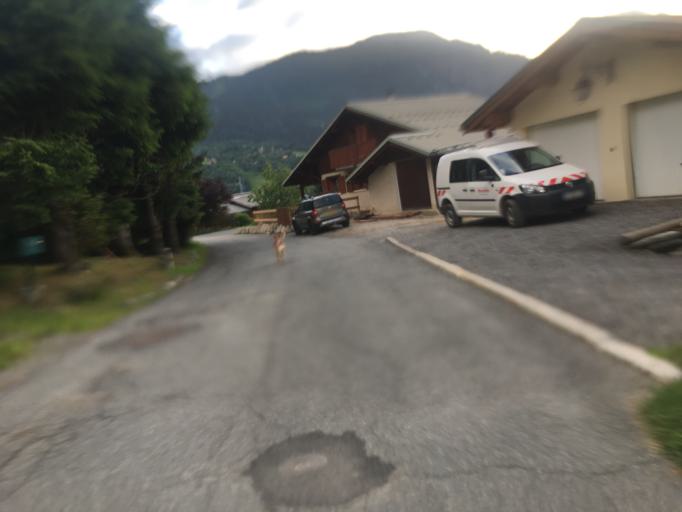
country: FR
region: Rhone-Alpes
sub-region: Departement de la Haute-Savoie
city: Les Houches
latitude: 45.8927
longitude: 6.8033
